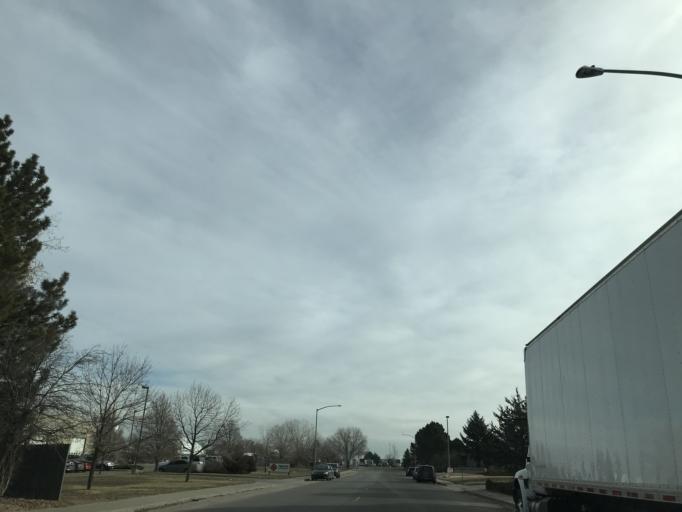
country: US
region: Colorado
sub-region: Adams County
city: Commerce City
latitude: 39.7751
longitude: -104.9019
